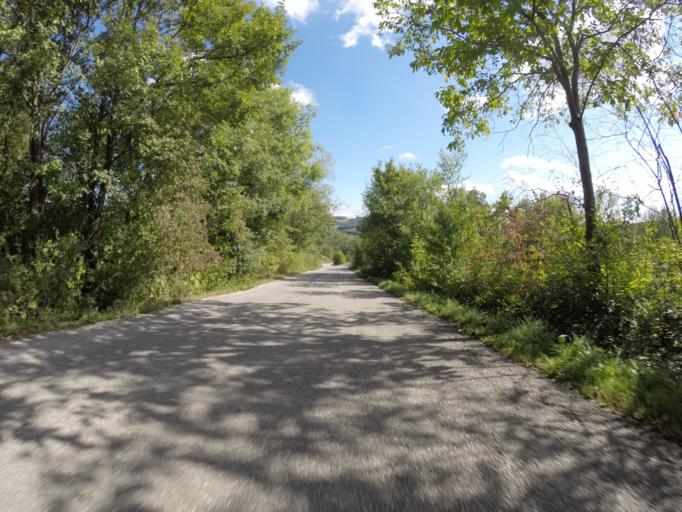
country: CZ
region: Zlin
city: Strani
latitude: 48.8390
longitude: 17.7536
